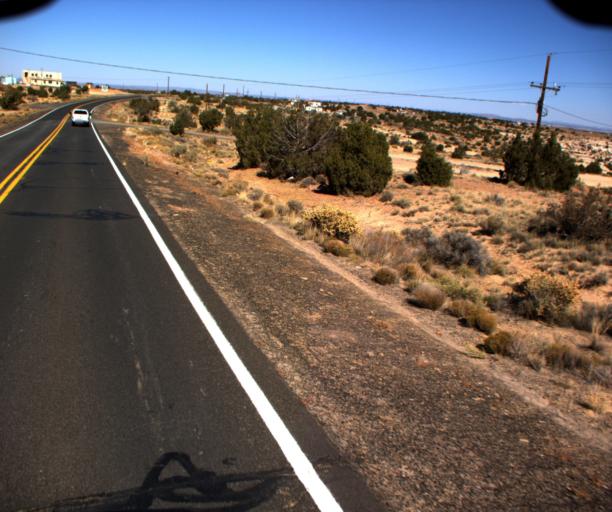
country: US
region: Arizona
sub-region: Navajo County
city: First Mesa
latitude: 35.8254
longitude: -110.5324
